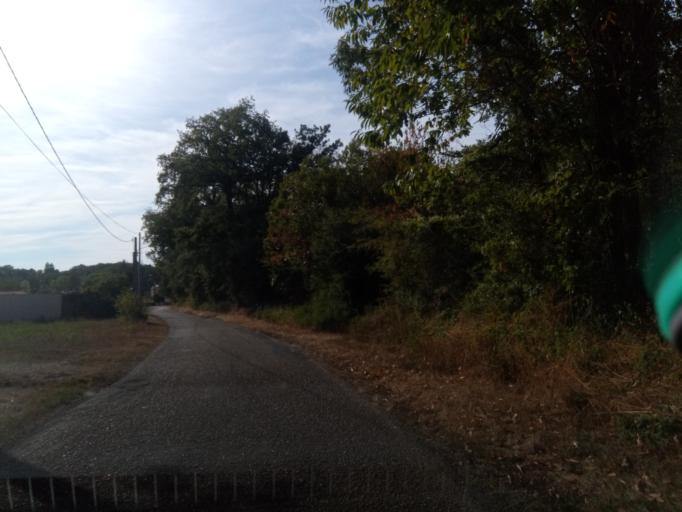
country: FR
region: Poitou-Charentes
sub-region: Departement de la Vienne
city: Saulge
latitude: 46.4032
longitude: 0.8825
